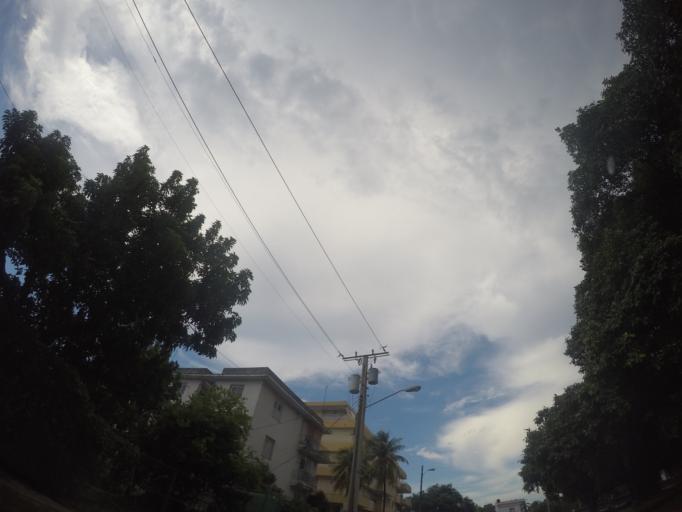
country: CU
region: La Habana
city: Havana
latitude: 23.1217
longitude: -82.4237
